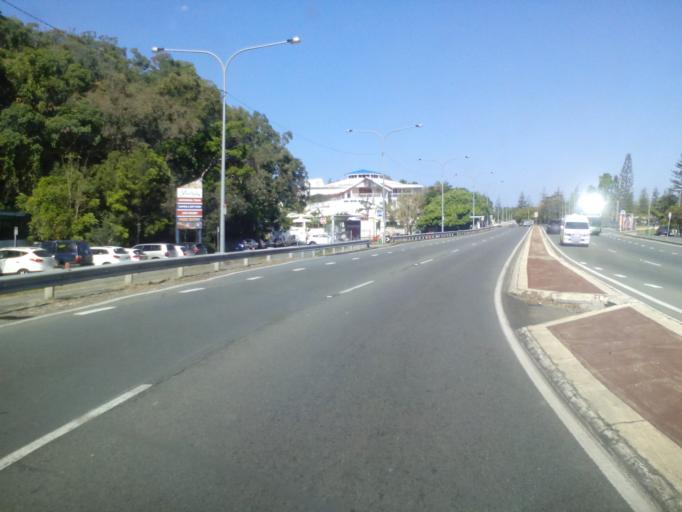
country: AU
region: Queensland
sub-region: Gold Coast
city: Palm Beach
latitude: -28.0966
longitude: 153.4547
